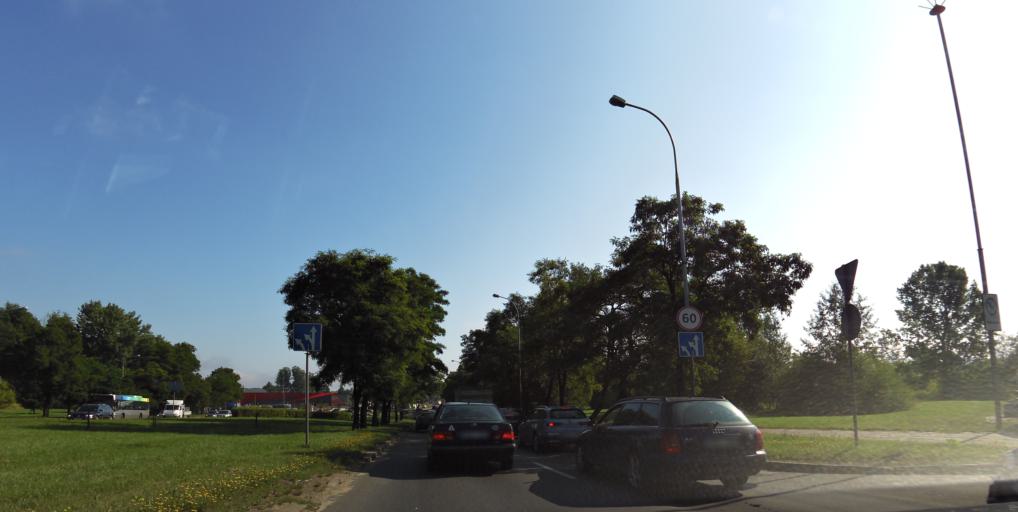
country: LT
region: Vilnius County
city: Seskine
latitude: 54.7027
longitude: 25.2647
